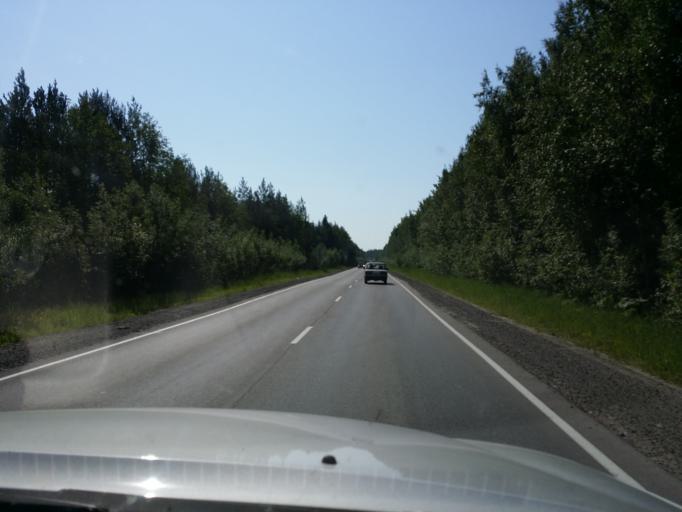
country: RU
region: Tomsk
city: Strezhevoy
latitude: 60.7525
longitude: 77.5052
